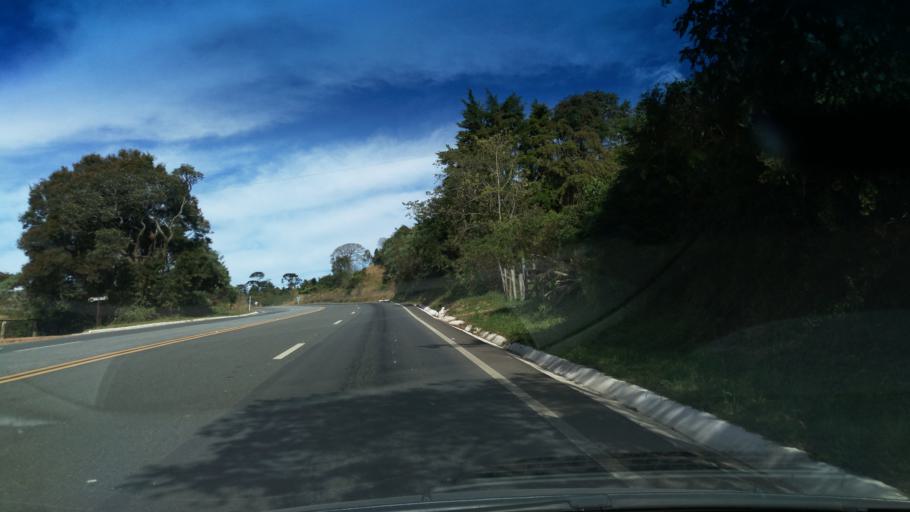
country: BR
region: Minas Gerais
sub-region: Borda Da Mata
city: Borda da Mata
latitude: -22.1223
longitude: -46.1807
